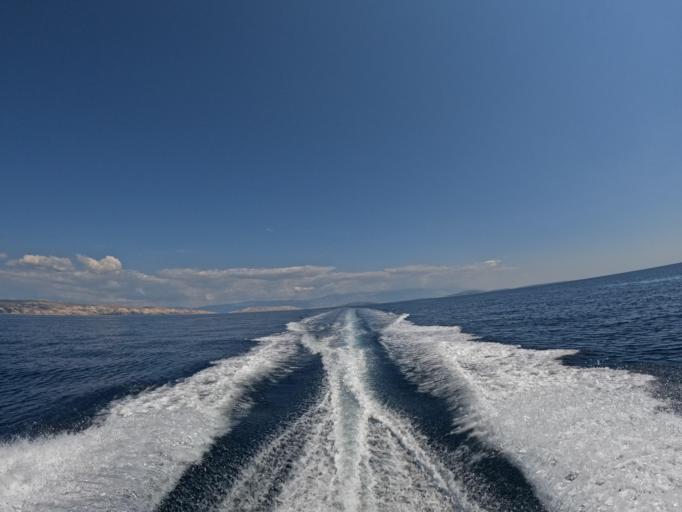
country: HR
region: Primorsko-Goranska
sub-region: Grad Krk
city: Krk
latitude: 44.9240
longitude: 14.5493
